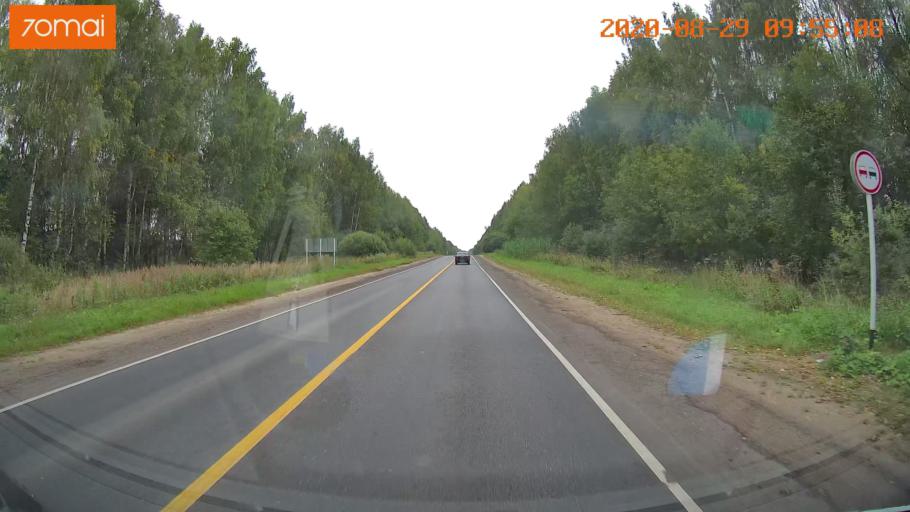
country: RU
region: Ivanovo
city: Zarechnyy
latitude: 57.4228
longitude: 42.2553
